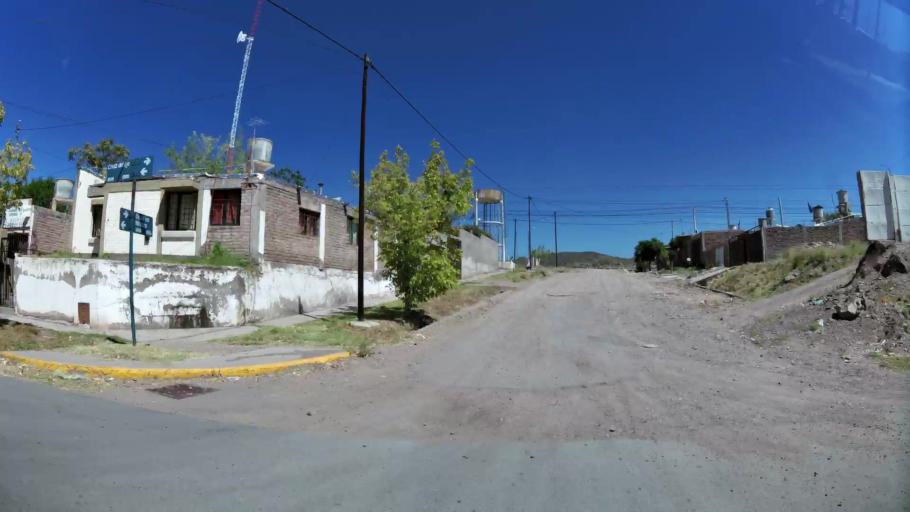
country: AR
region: Mendoza
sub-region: Departamento de Godoy Cruz
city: Godoy Cruz
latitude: -32.9392
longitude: -68.8756
